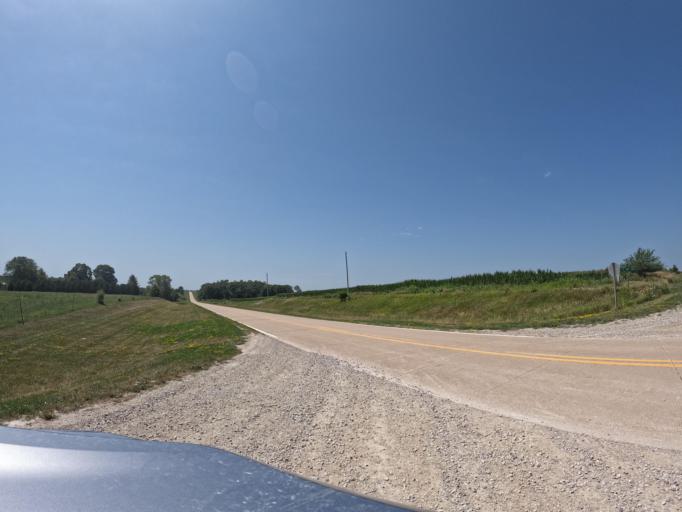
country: US
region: Iowa
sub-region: Henry County
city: Mount Pleasant
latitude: 40.8792
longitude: -91.5605
